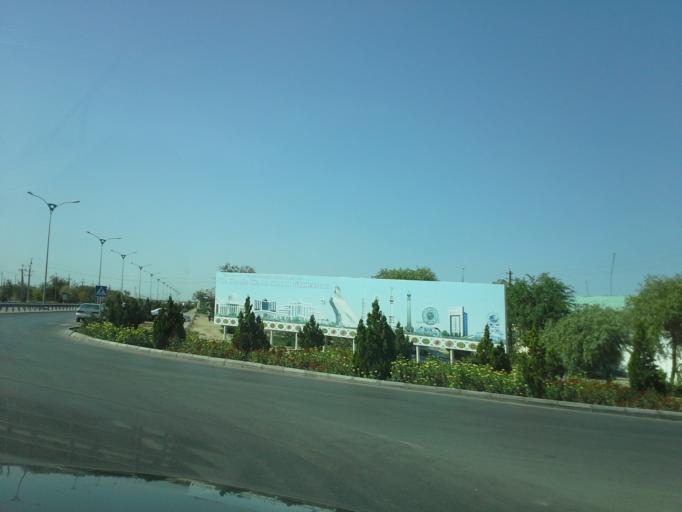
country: TM
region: Dasoguz
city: Dasoguz
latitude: 41.8470
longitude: 59.9332
